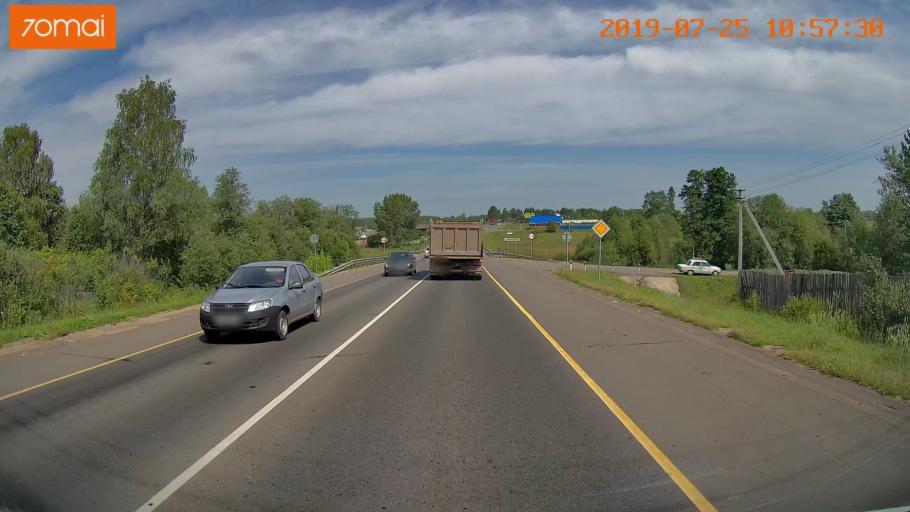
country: RU
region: Ivanovo
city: Furmanov
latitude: 57.1608
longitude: 41.0691
